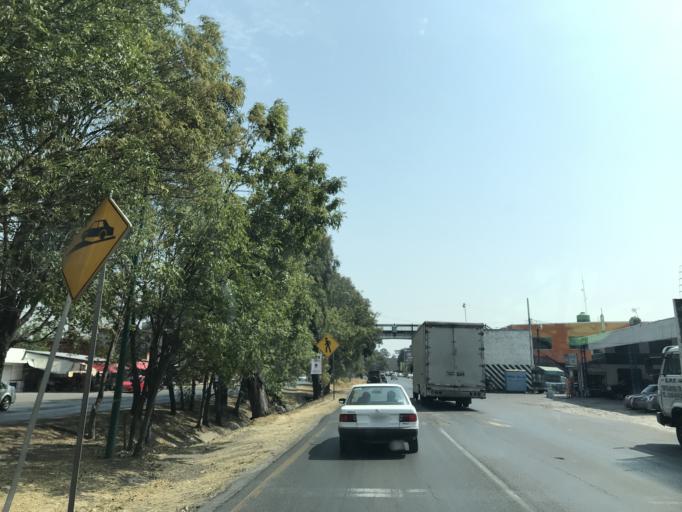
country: MX
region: Tlaxcala
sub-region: Apetatitlan de Antonio Carvajal
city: Tlatempan
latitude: 19.3314
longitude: -98.1983
